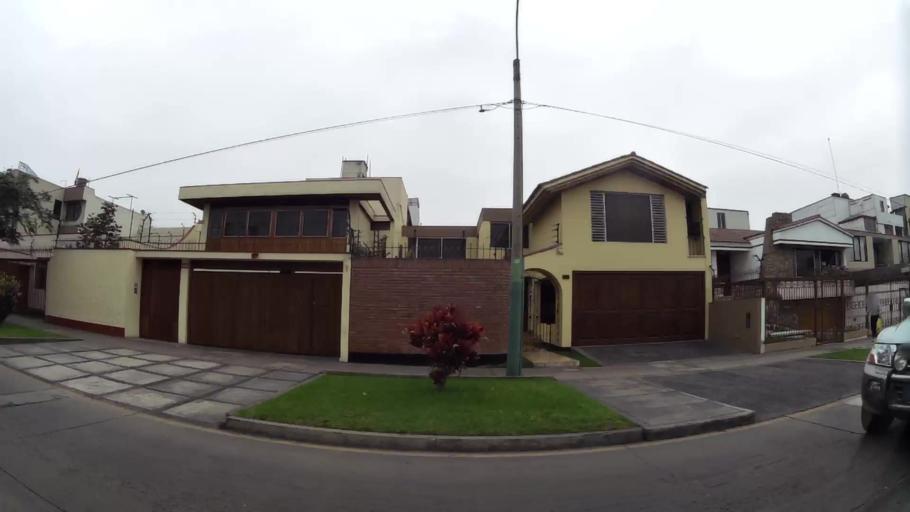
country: PE
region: Lima
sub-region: Lima
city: San Luis
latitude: -12.0897
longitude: -76.9943
